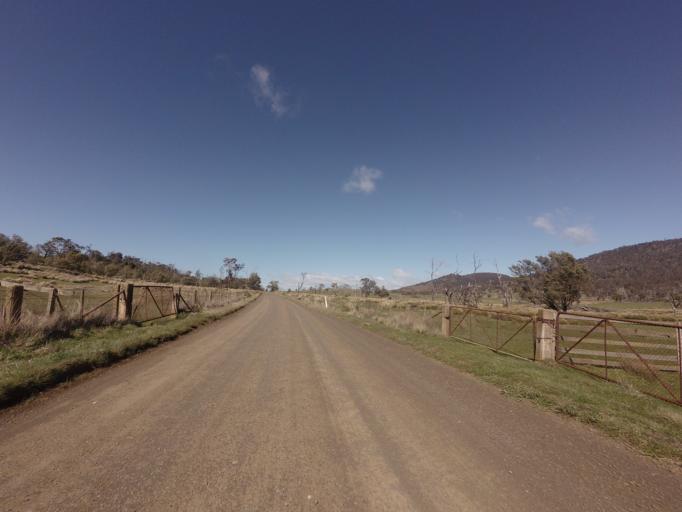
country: AU
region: Tasmania
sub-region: Northern Midlands
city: Evandale
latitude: -41.9354
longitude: 147.4193
